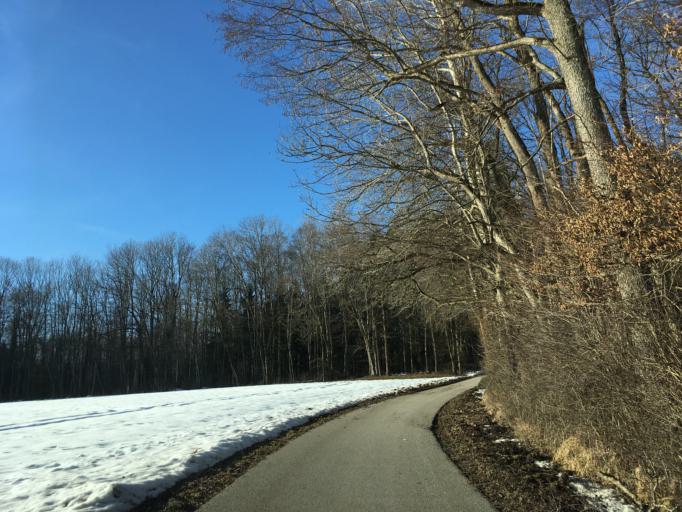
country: DE
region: Bavaria
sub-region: Upper Bavaria
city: Steinhoring
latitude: 48.1033
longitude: 12.0158
